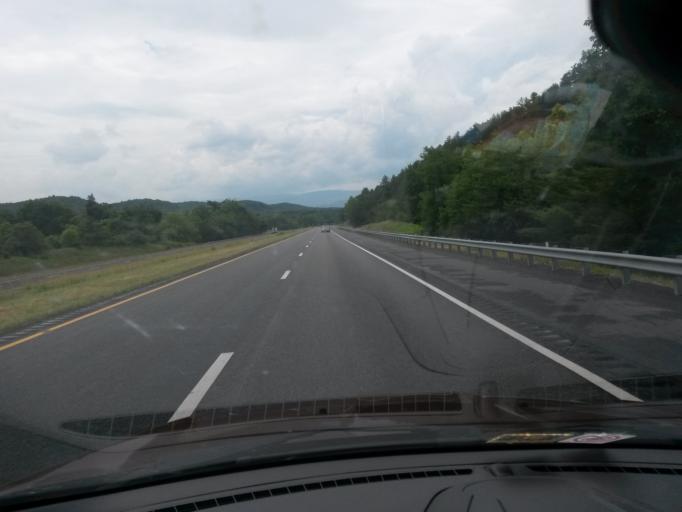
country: US
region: Virginia
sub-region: Alleghany County
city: Clifton Forge
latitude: 37.8020
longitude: -79.7348
